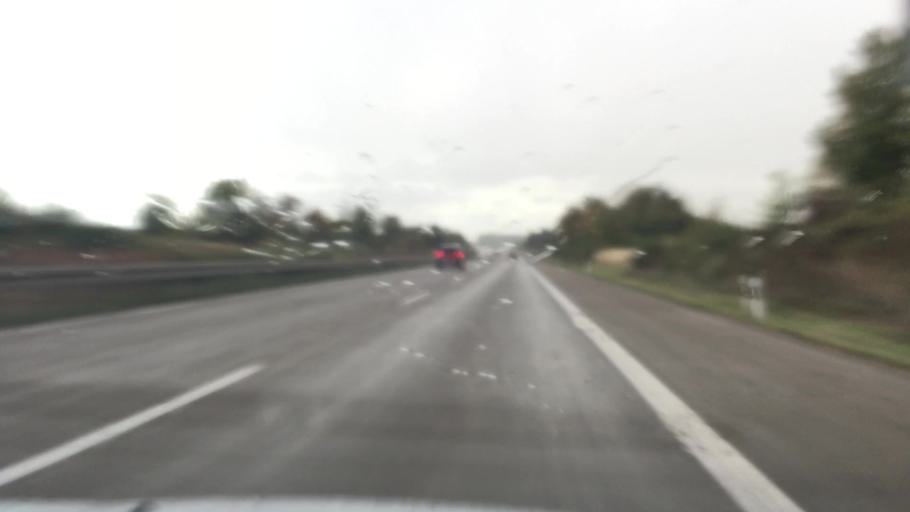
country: DE
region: Saxony-Anhalt
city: Biere
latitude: 51.9769
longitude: 11.6701
